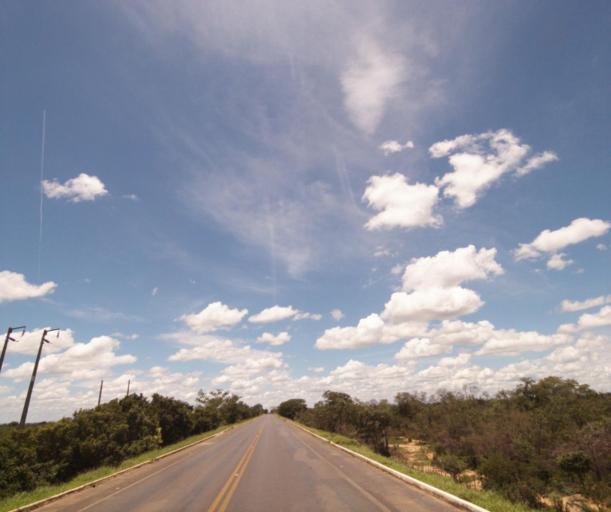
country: BR
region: Bahia
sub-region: Bom Jesus Da Lapa
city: Bom Jesus da Lapa
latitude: -13.2558
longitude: -43.4408
